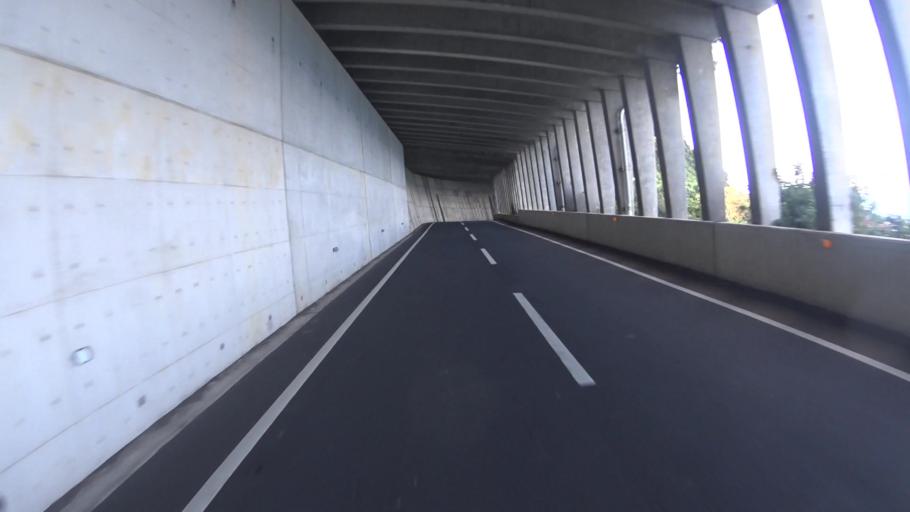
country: JP
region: Kyoto
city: Miyazu
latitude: 35.7624
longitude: 135.2391
